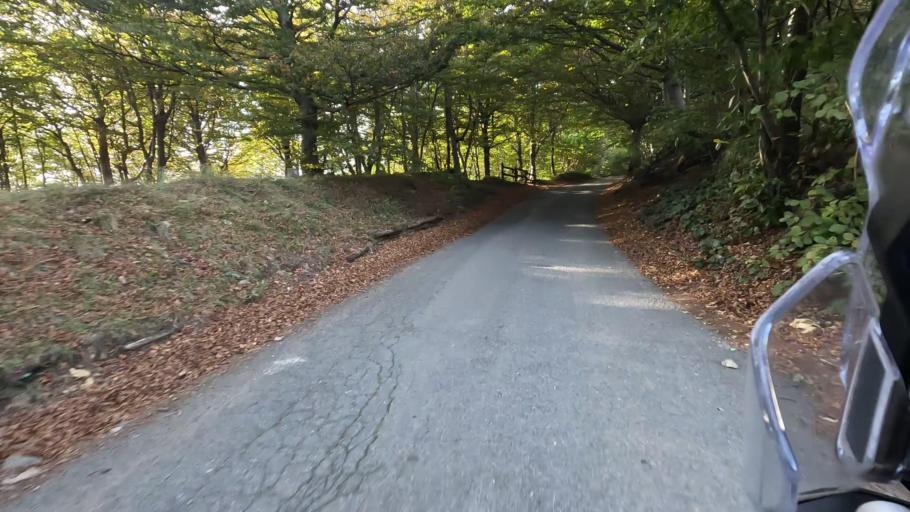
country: IT
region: Liguria
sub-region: Provincia di Genova
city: Sciarborasca
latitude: 44.4279
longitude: 8.5865
